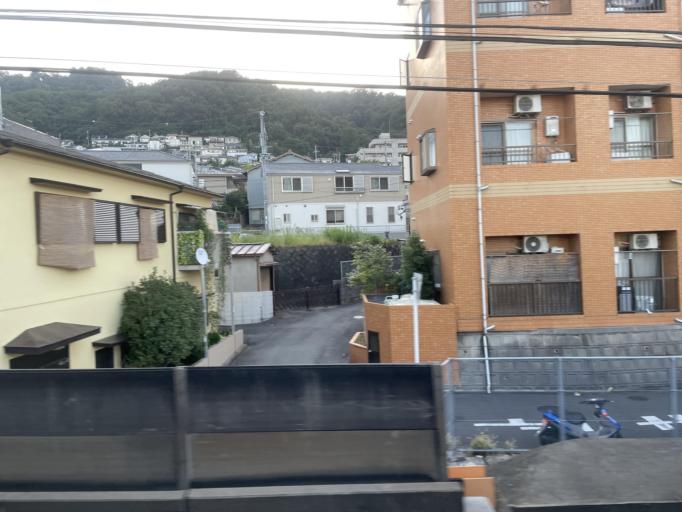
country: JP
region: Osaka
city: Daitocho
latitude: 34.6664
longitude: 135.6472
